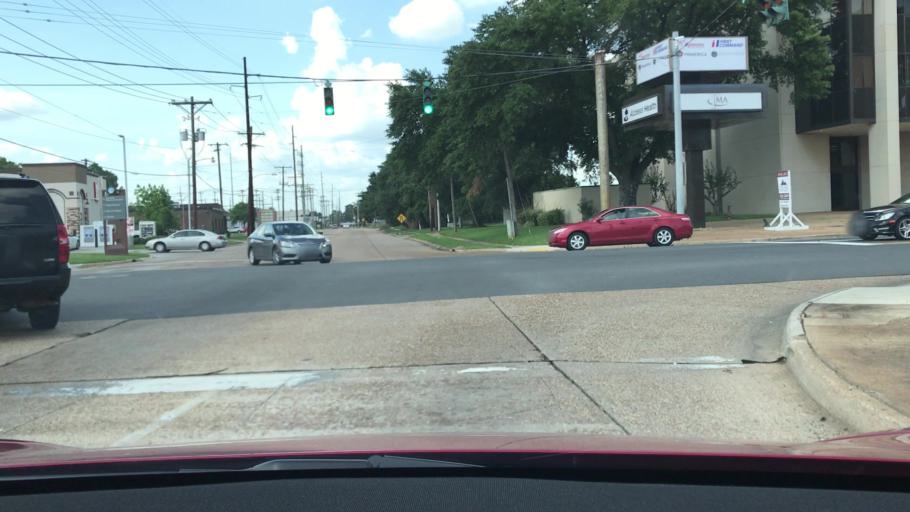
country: US
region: Louisiana
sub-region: Bossier Parish
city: Bossier City
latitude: 32.5156
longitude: -93.7261
